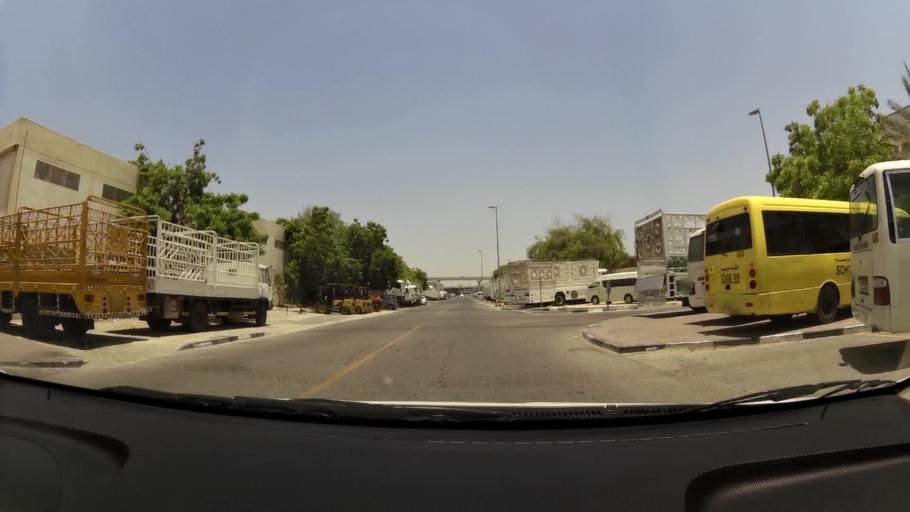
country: AE
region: Ash Shariqah
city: Sharjah
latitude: 25.2680
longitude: 55.3357
